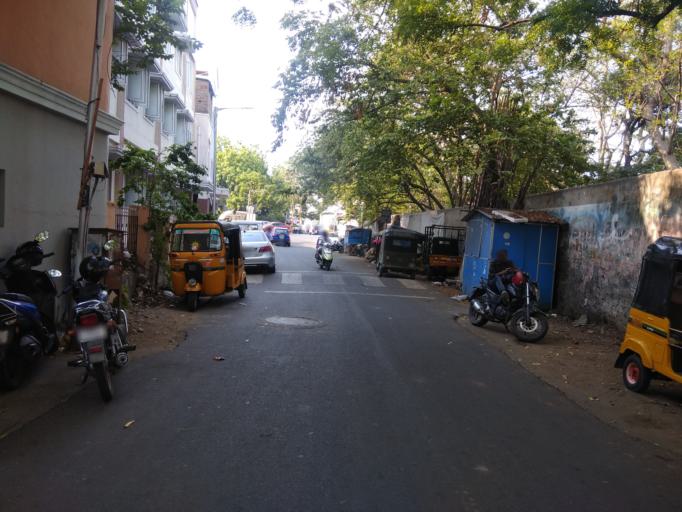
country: IN
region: Tamil Nadu
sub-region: Chennai
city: Gandhi Nagar
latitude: 13.0258
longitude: 80.2328
